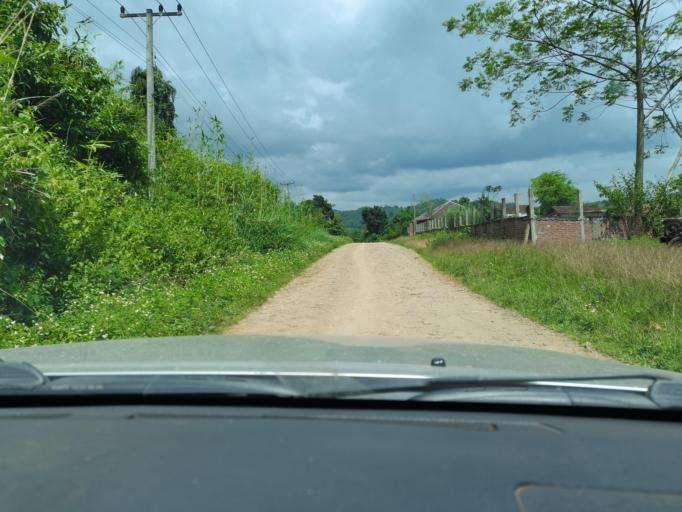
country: LA
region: Loungnamtha
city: Muang Long
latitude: 20.6804
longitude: 101.0558
